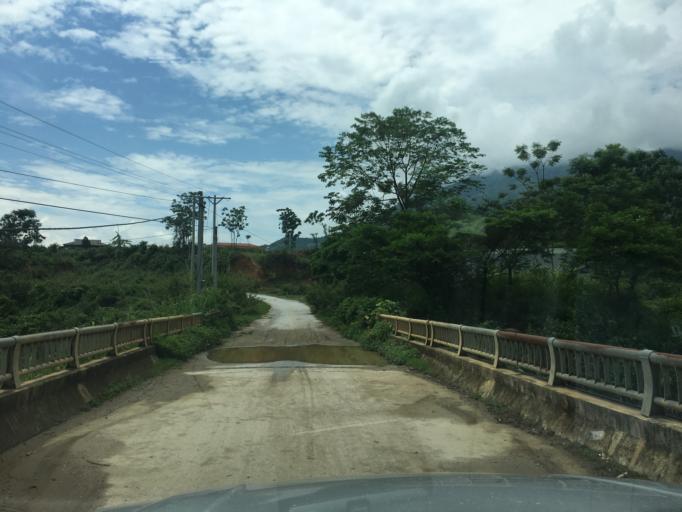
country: VN
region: Yen Bai
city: Son Thinh
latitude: 21.6574
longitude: 104.5063
